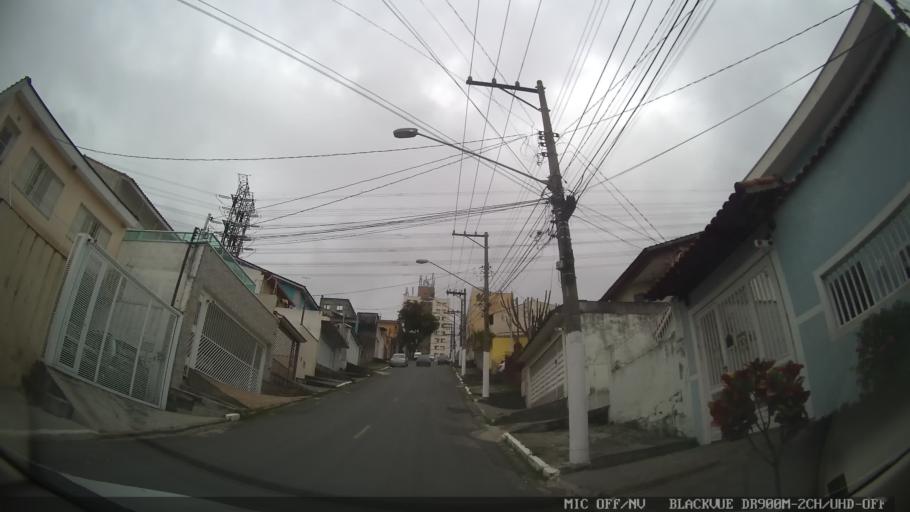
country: BR
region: Sao Paulo
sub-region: Sao Paulo
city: Sao Paulo
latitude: -23.5018
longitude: -46.6044
